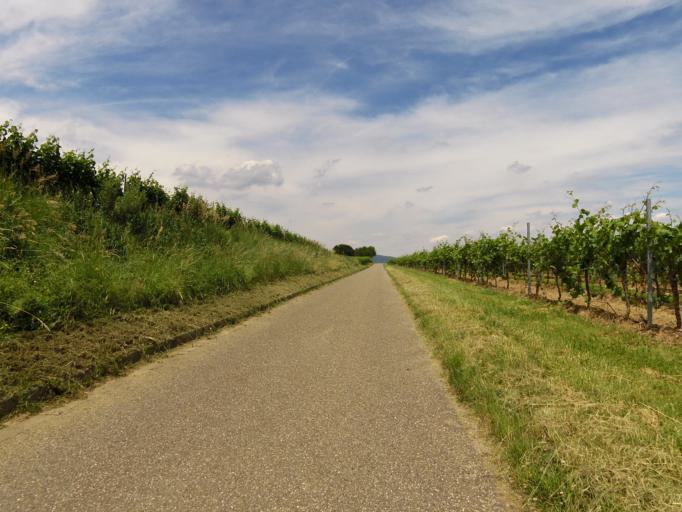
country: DE
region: Rheinland-Pfalz
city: Walsheim
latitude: 49.2383
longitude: 8.1199
